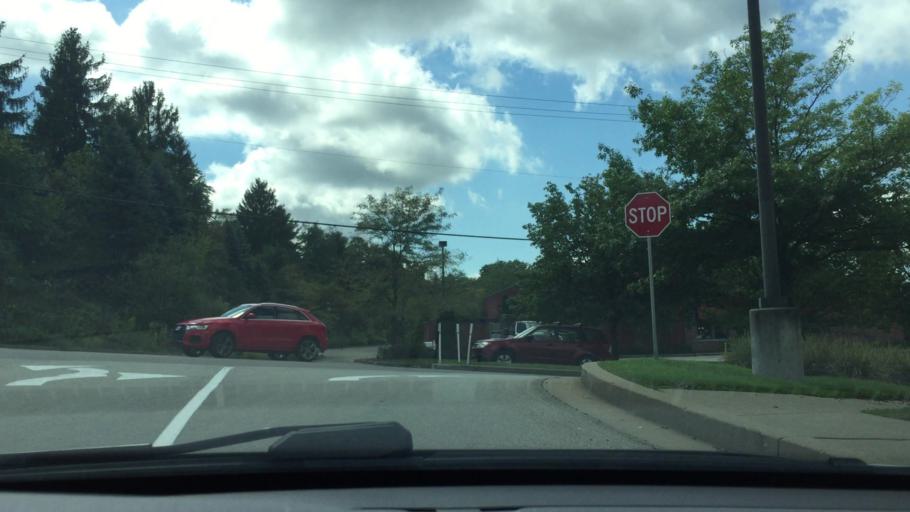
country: US
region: Pennsylvania
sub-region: Washington County
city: Thompsonville
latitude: 40.2656
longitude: -80.1284
